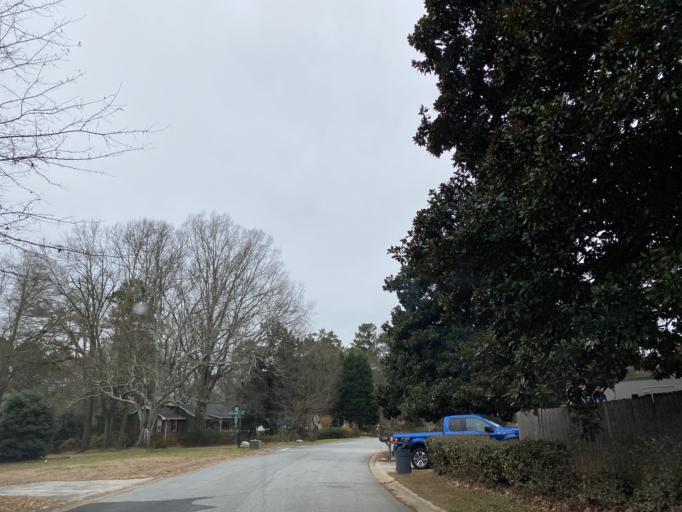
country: US
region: Georgia
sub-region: Cobb County
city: Fair Oaks
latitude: 33.9167
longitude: -84.5670
